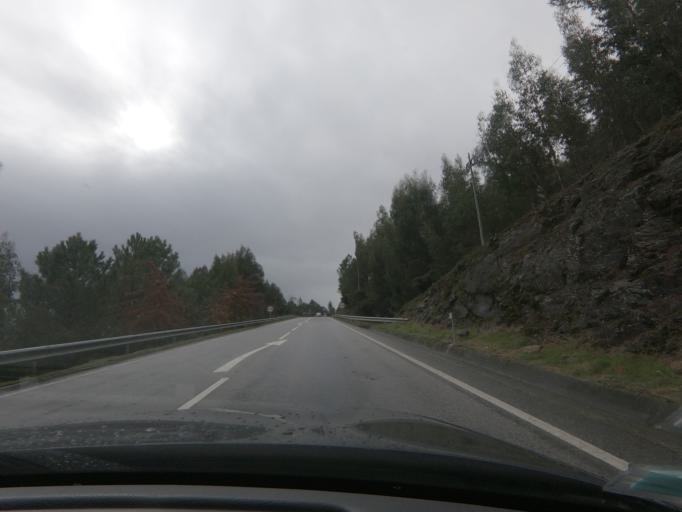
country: PT
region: Braga
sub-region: Celorico de Basto
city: Celorico de Basto
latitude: 41.3506
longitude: -8.0161
